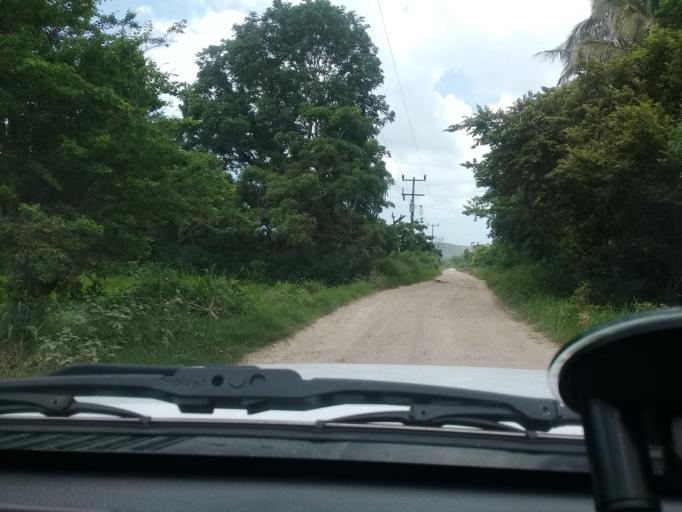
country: MX
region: Veracruz
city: Panuco
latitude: 22.1284
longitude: -98.0588
